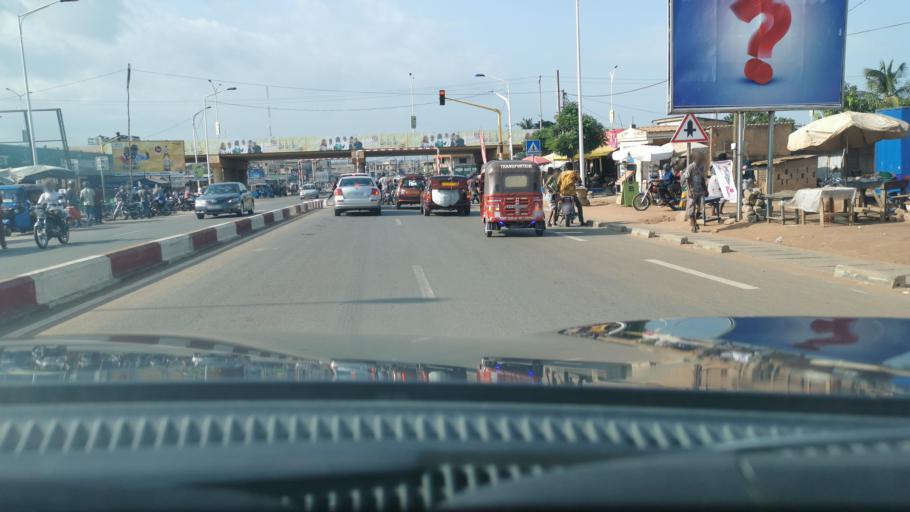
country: TG
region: Maritime
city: Lome
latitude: 6.2102
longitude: 1.2443
